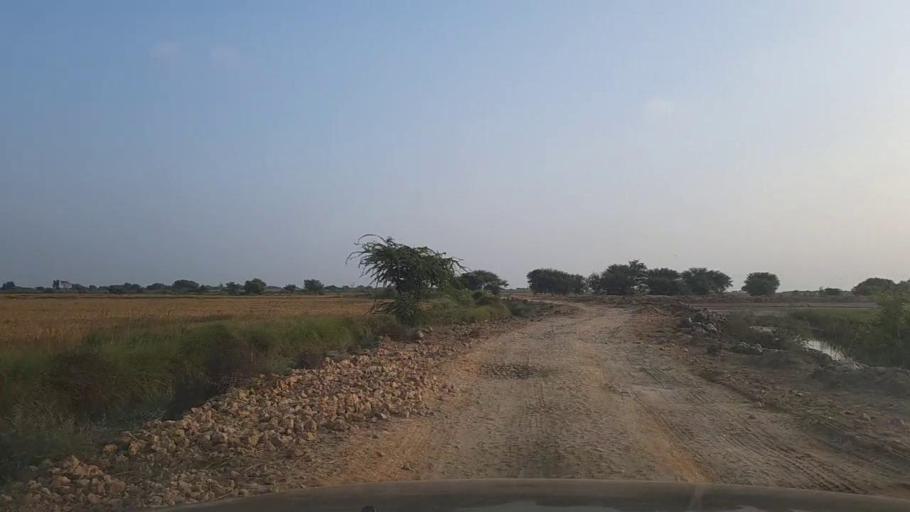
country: PK
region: Sindh
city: Jati
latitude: 24.5383
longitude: 68.3605
